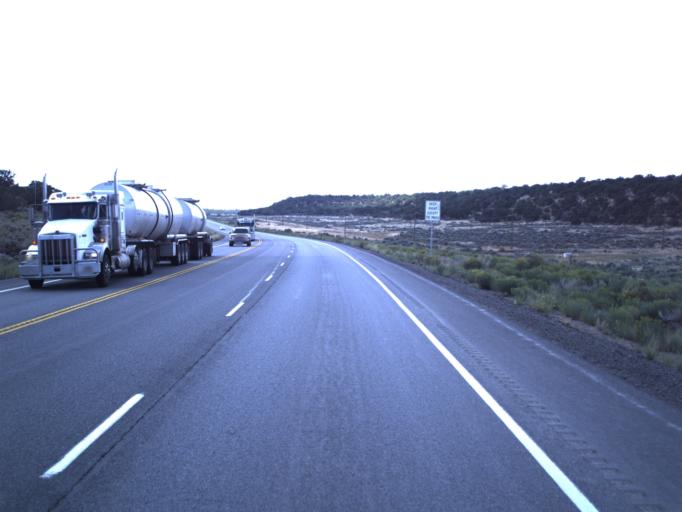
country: US
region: Utah
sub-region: Duchesne County
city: Duchesne
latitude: 40.1795
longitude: -110.6037
